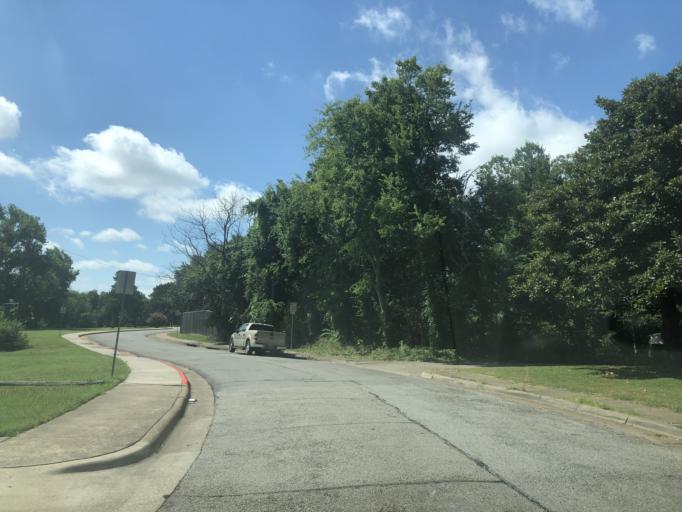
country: US
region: Texas
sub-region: Dallas County
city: Duncanville
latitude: 32.6558
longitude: -96.9220
